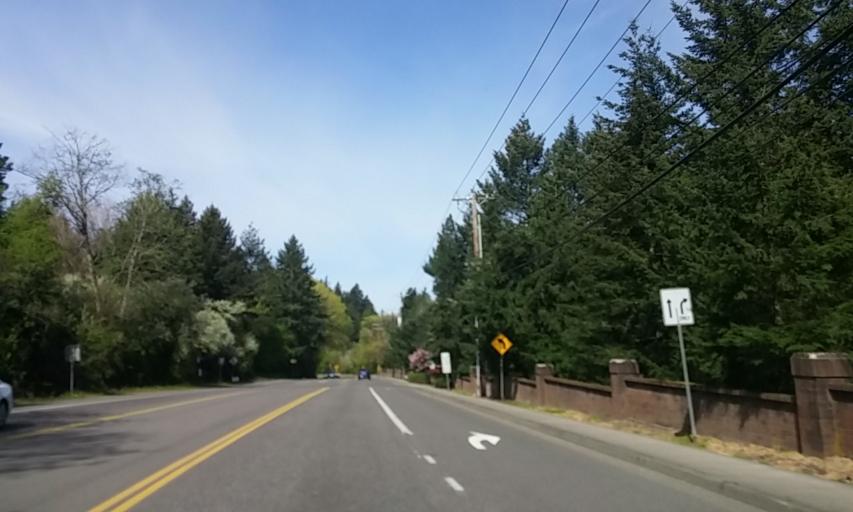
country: US
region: Oregon
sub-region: Washington County
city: West Haven-Sylvan
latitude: 45.5161
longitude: -122.7481
